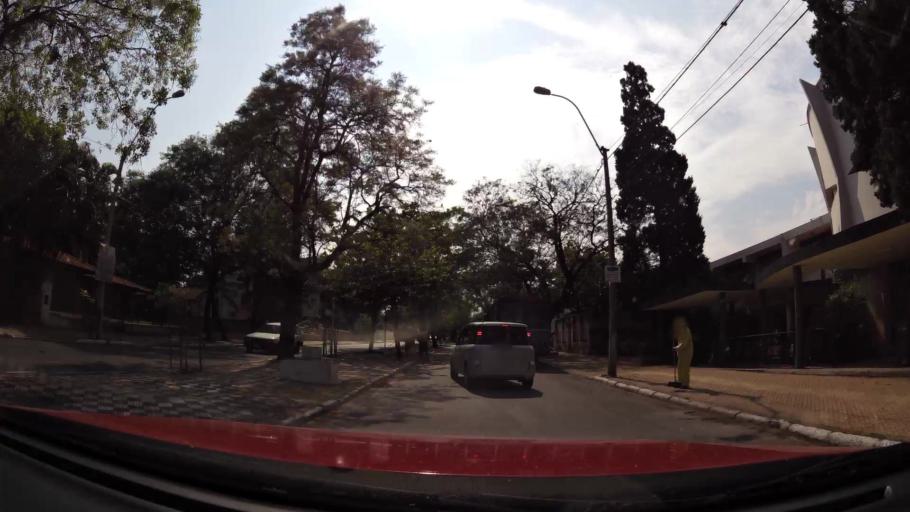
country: PY
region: Presidente Hayes
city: Nanawa
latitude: -25.2897
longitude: -57.6598
